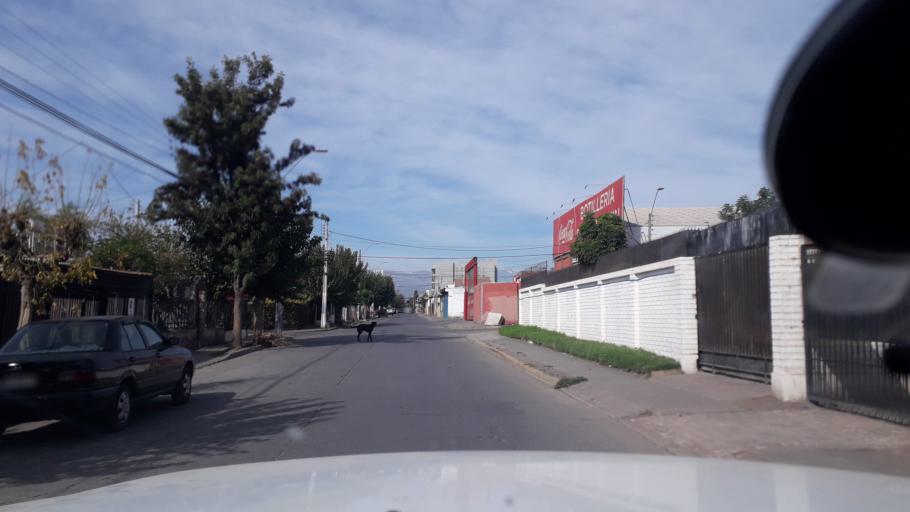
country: CL
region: Valparaiso
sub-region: Provincia de San Felipe
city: San Felipe
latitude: -32.7495
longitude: -70.7326
